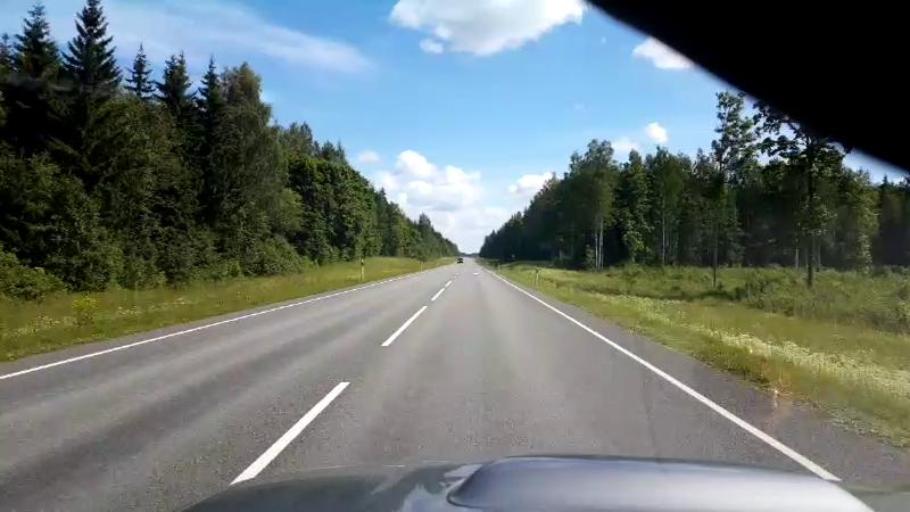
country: EE
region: Jaervamaa
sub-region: Jaerva-Jaani vald
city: Jarva-Jaani
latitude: 59.1810
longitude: 25.7867
